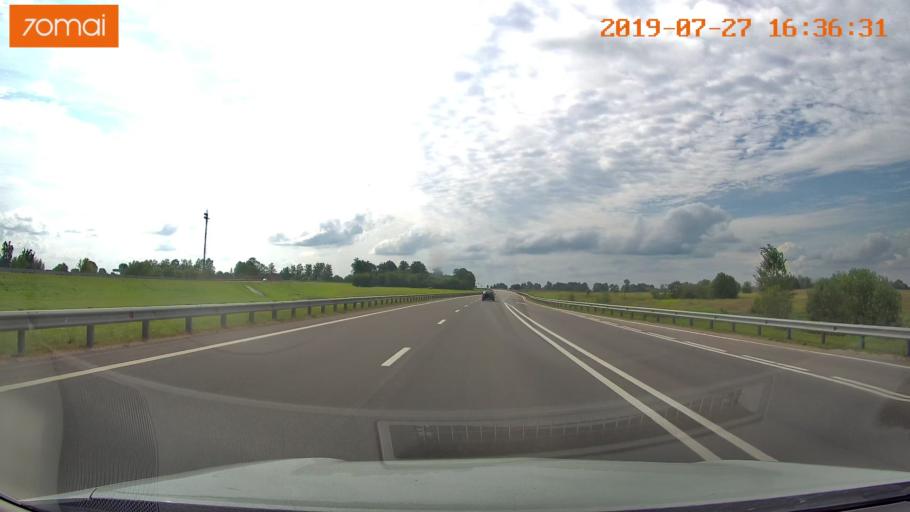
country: RU
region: Kaliningrad
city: Gvardeysk
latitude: 54.6483
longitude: 21.2809
